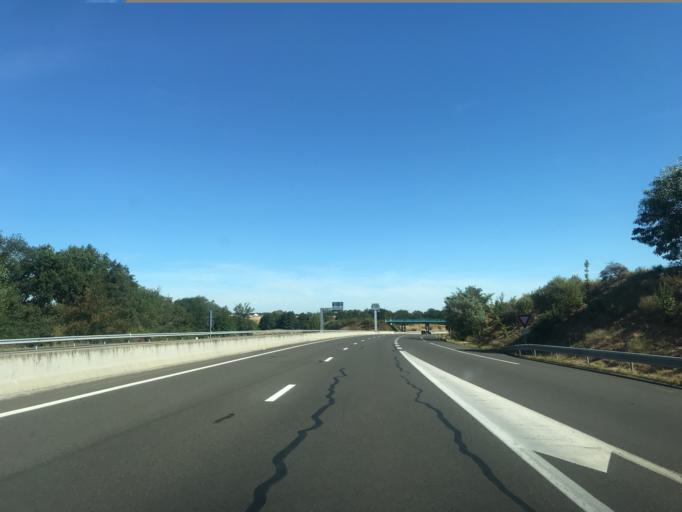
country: FR
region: Auvergne
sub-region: Departement de l'Allier
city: Premilhat
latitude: 46.3348
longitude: 2.5362
